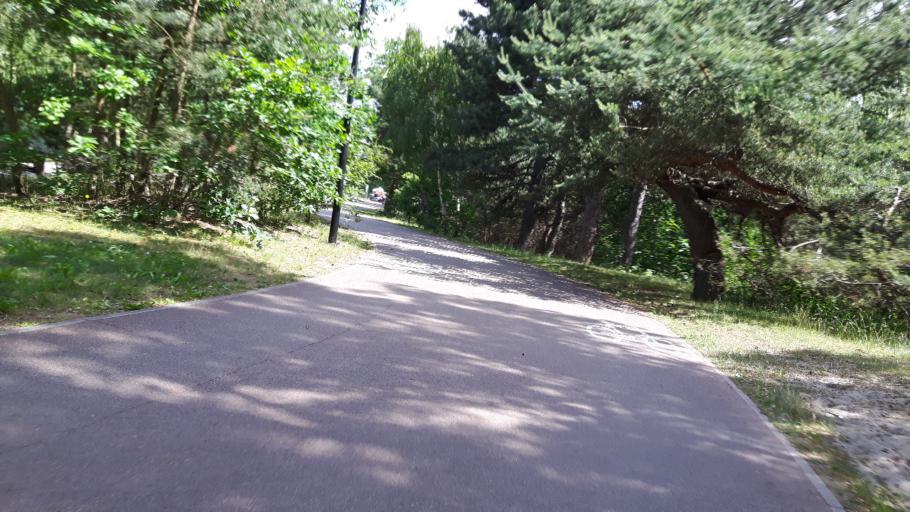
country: PL
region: Pomeranian Voivodeship
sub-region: Gdansk
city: Gdansk
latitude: 54.4141
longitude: 18.6218
